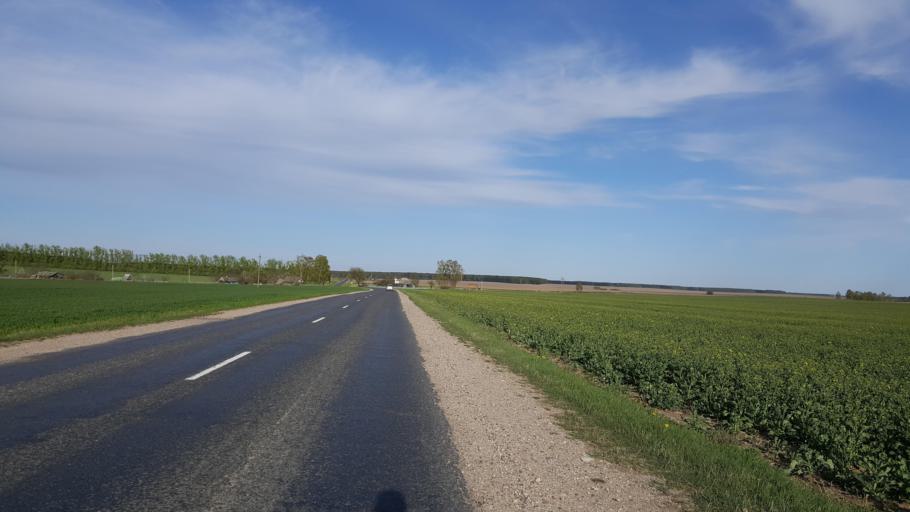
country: BY
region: Brest
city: Vysokaye
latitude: 52.4019
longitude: 23.5274
